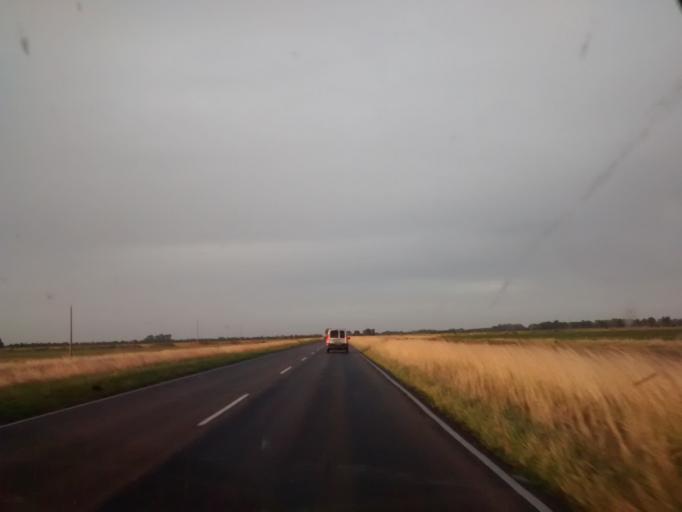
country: AR
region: Buenos Aires
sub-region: Partido de General Belgrano
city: General Belgrano
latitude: -35.9102
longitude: -58.6191
